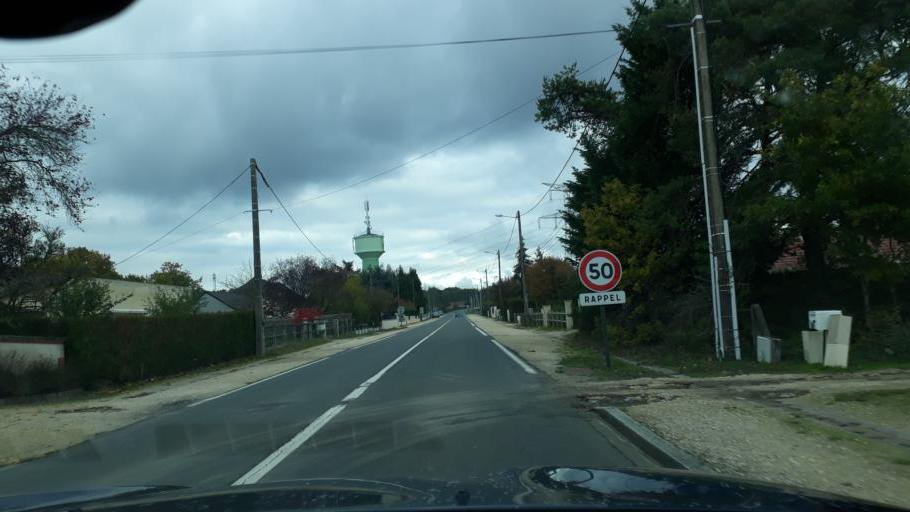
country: FR
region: Centre
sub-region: Departement du Loiret
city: Bray-en-Val
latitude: 47.8183
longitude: 2.4064
